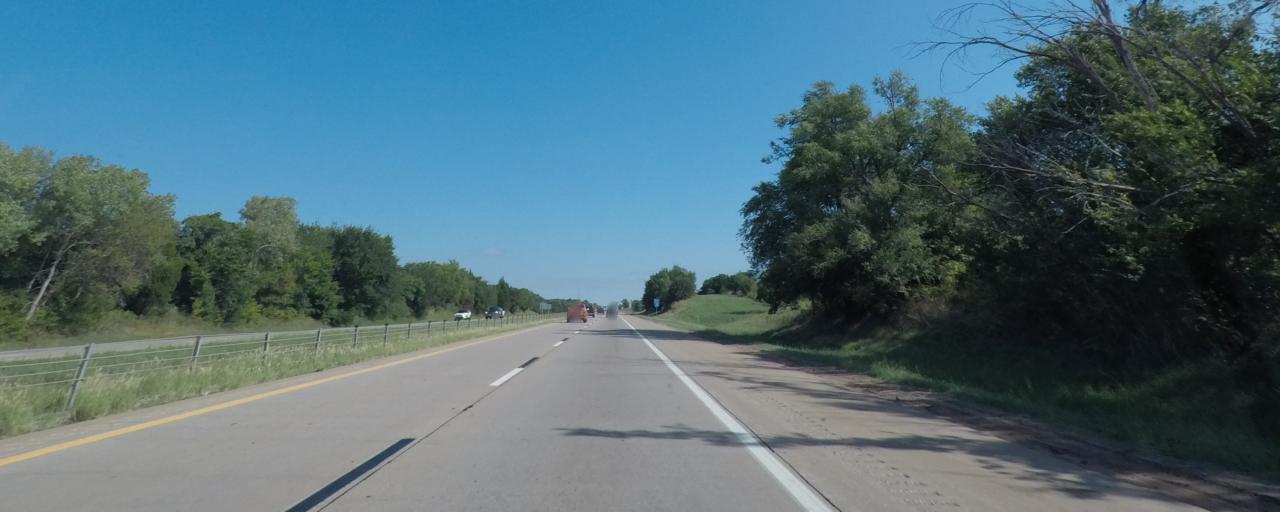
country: US
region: Oklahoma
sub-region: Oklahoma County
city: Edmond
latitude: 35.7307
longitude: -97.4162
